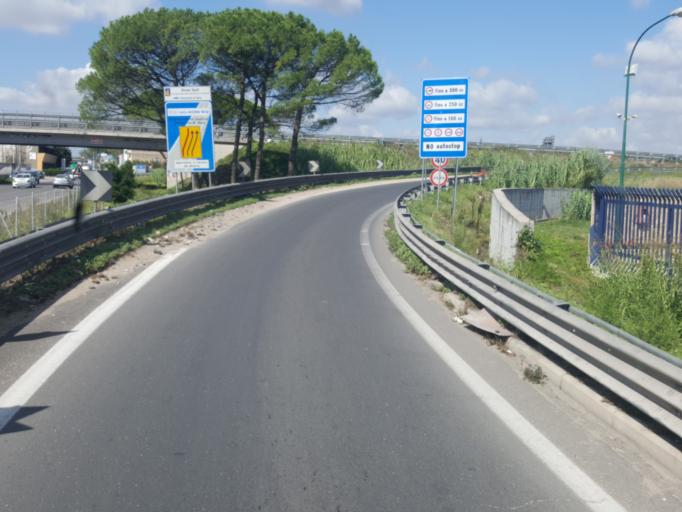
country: IT
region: Campania
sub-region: Provincia di Napoli
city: Cimitile
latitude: 40.9334
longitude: 14.5008
